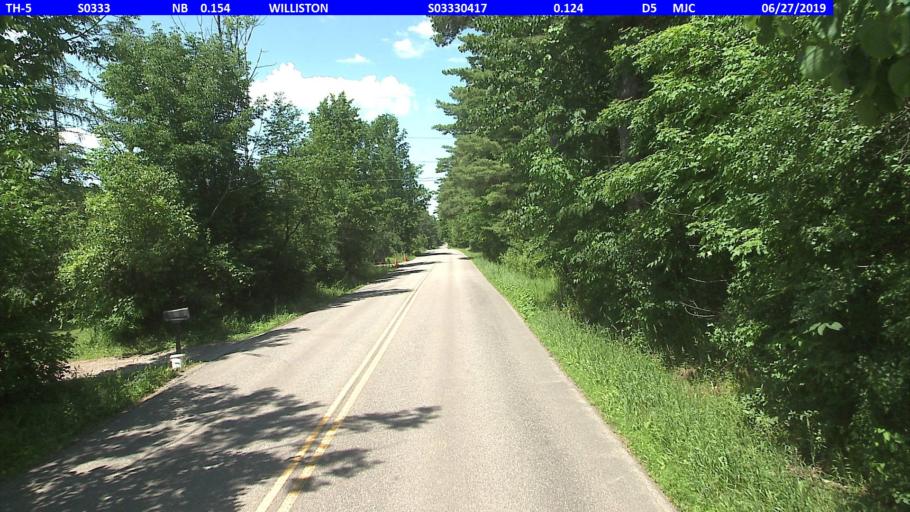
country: US
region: Vermont
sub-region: Chittenden County
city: South Burlington
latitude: 44.4033
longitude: -73.1407
